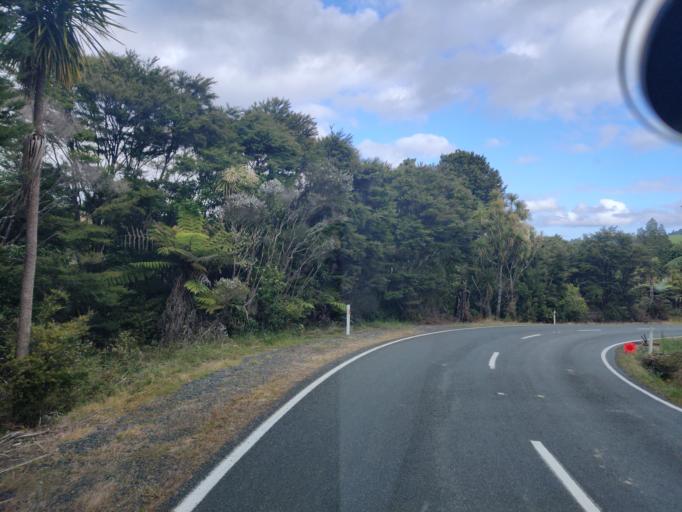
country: NZ
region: Northland
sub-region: Whangarei
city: Ngunguru
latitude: -35.5827
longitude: 174.4238
